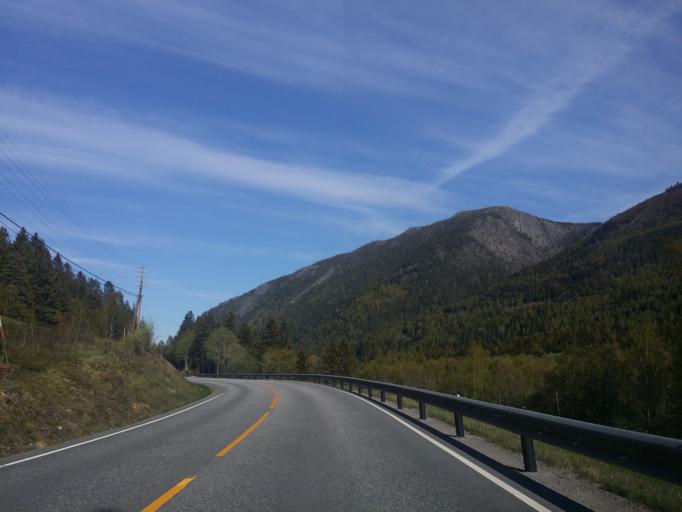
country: NO
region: Telemark
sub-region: Hjartdal
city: Sauland
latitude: 59.6089
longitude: 8.7632
